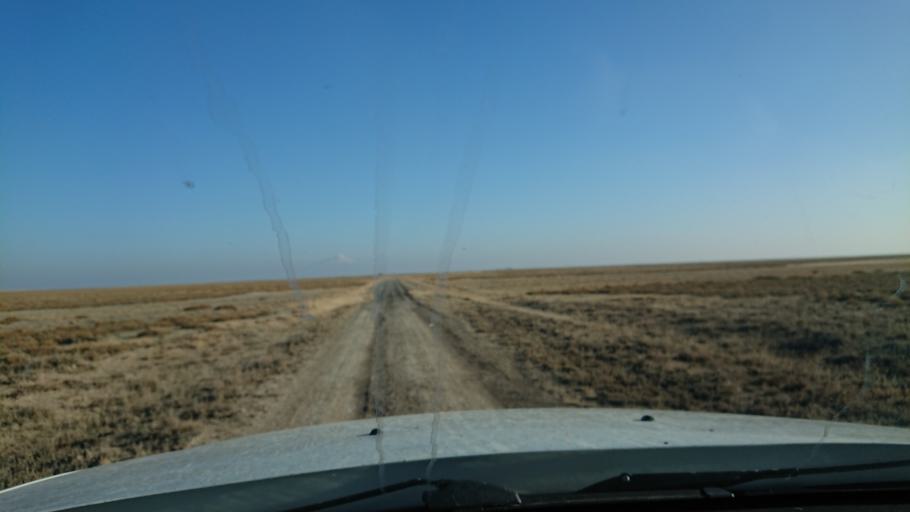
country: TR
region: Aksaray
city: Sultanhani
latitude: 38.4016
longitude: 33.5795
